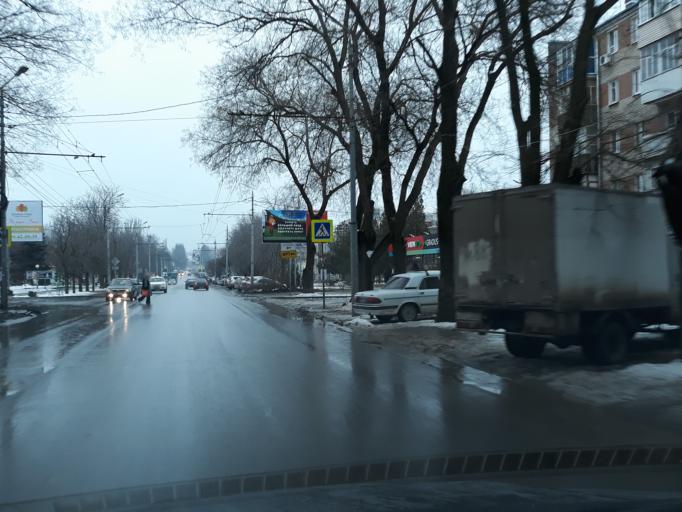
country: RU
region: Rostov
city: Taganrog
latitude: 47.2546
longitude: 38.9179
